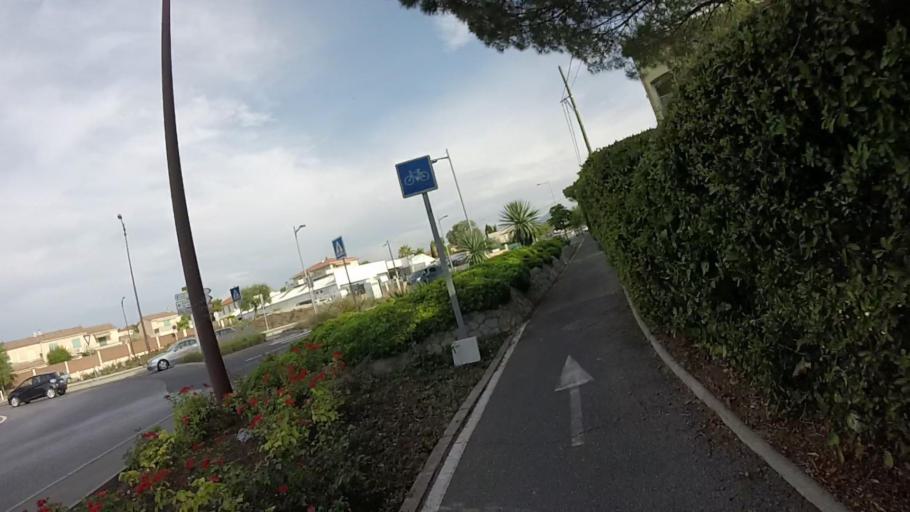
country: FR
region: Provence-Alpes-Cote d'Azur
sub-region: Departement des Alpes-Maritimes
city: Biot
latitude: 43.5969
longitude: 7.1141
